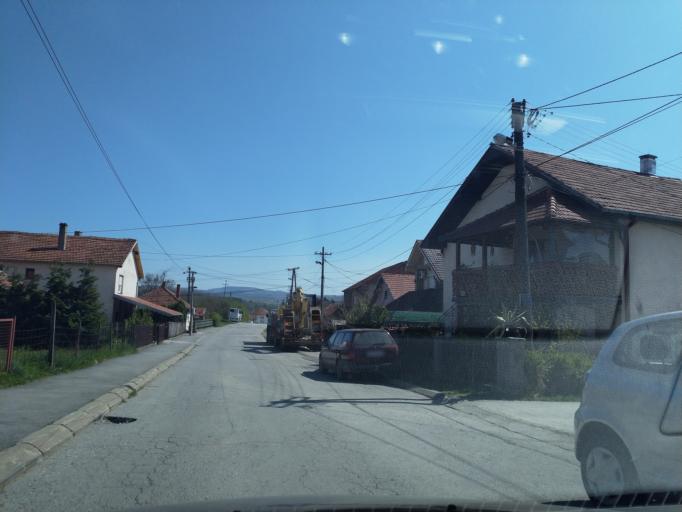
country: RS
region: Central Serbia
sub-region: Kolubarski Okrug
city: Valjevo
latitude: 44.2779
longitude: 19.8702
